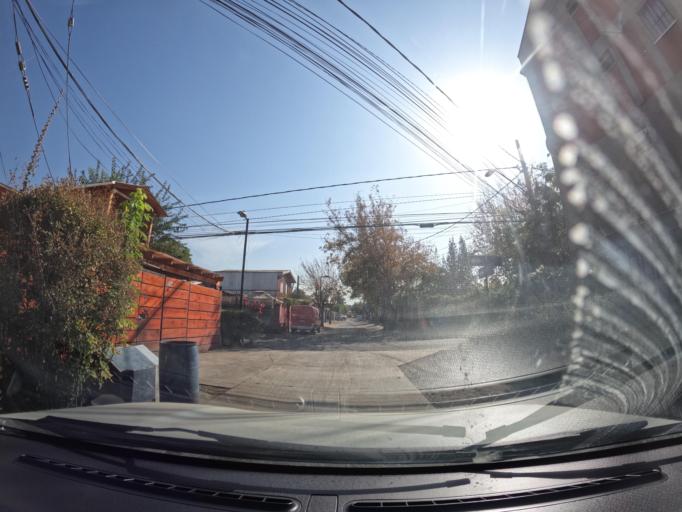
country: CL
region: Santiago Metropolitan
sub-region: Provincia de Santiago
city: Villa Presidente Frei, Nunoa, Santiago, Chile
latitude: -33.4640
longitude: -70.5621
